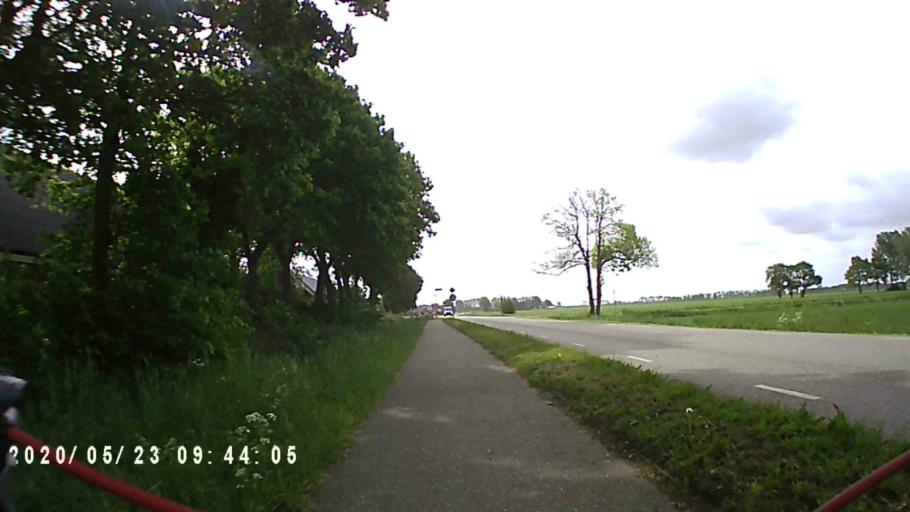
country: NL
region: Groningen
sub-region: Gemeente Slochteren
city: Slochteren
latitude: 53.2863
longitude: 6.7466
